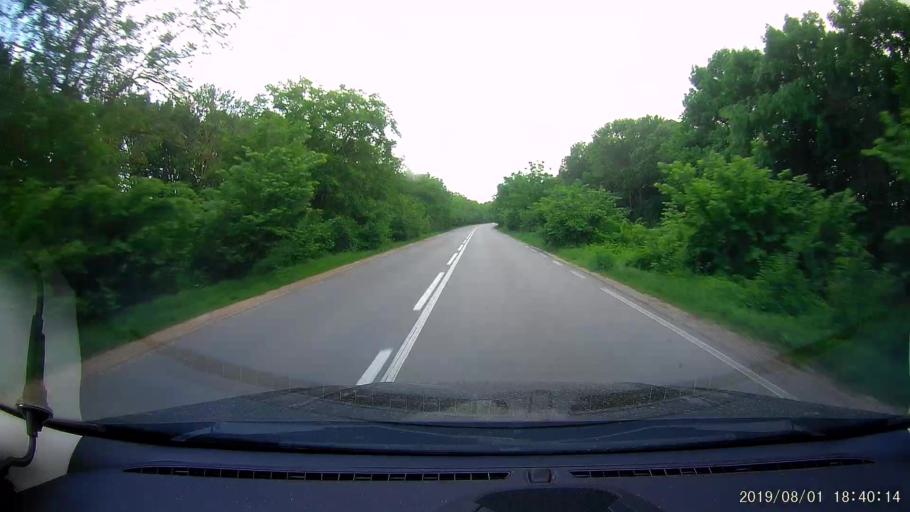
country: BG
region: Shumen
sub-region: Obshtina Khitrino
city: Gara Khitrino
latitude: 43.3712
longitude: 26.9200
